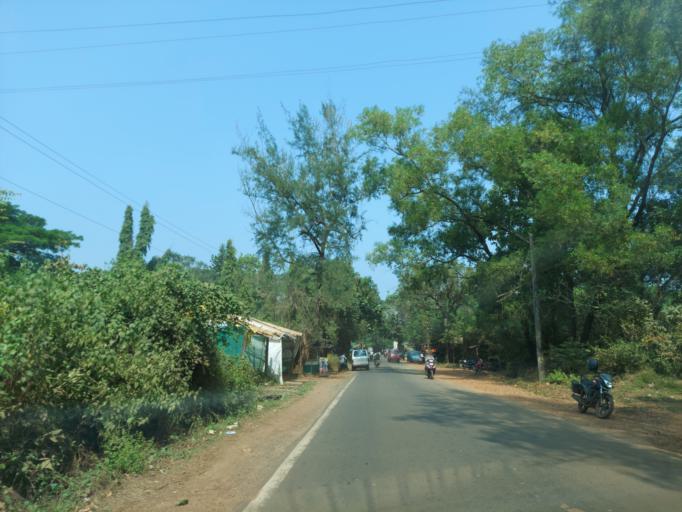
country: IN
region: Maharashtra
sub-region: Sindhudurg
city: Kudal
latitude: 15.9986
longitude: 73.6855
